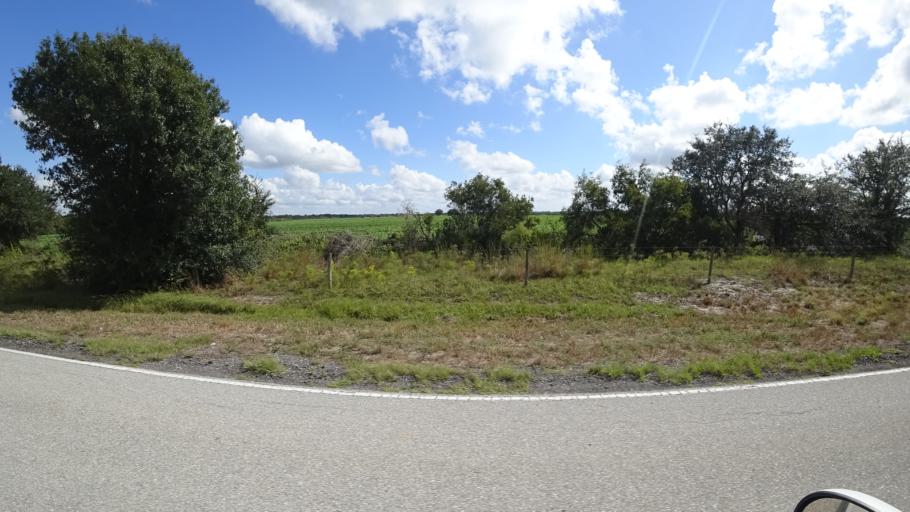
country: US
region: Florida
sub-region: Sarasota County
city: Lake Sarasota
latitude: 27.4234
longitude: -82.1332
